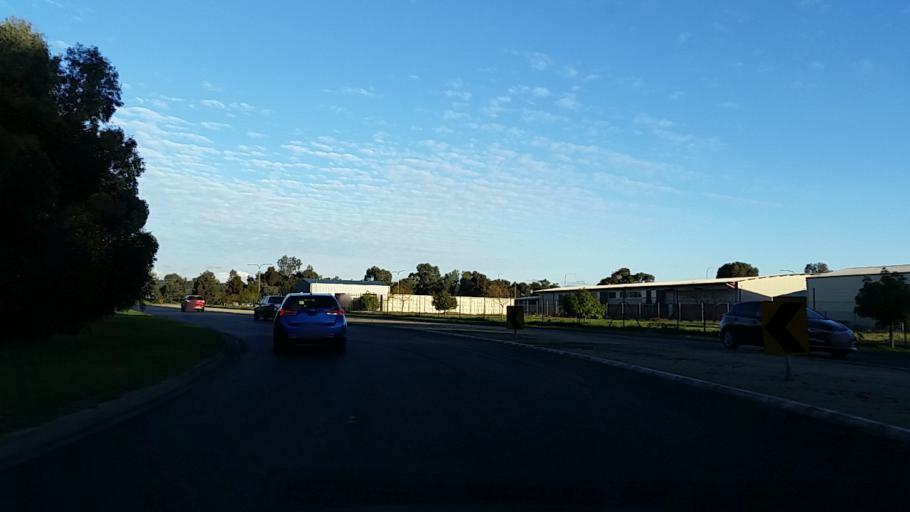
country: AU
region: South Australia
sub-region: Salisbury
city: Salisbury
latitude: -34.7500
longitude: 138.6454
